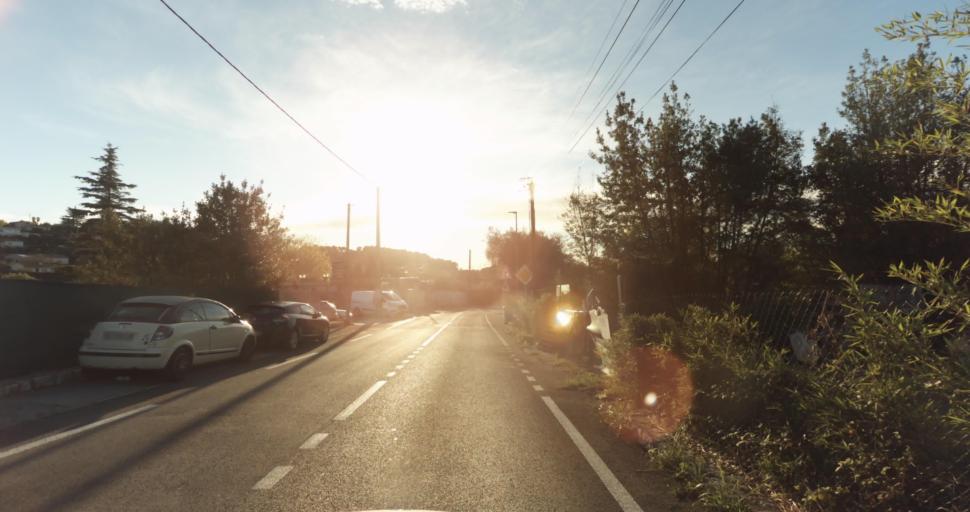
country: FR
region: Provence-Alpes-Cote d'Azur
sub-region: Departement des Alpes-Maritimes
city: Saint-Paul-de-Vence
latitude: 43.7136
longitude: 7.1283
